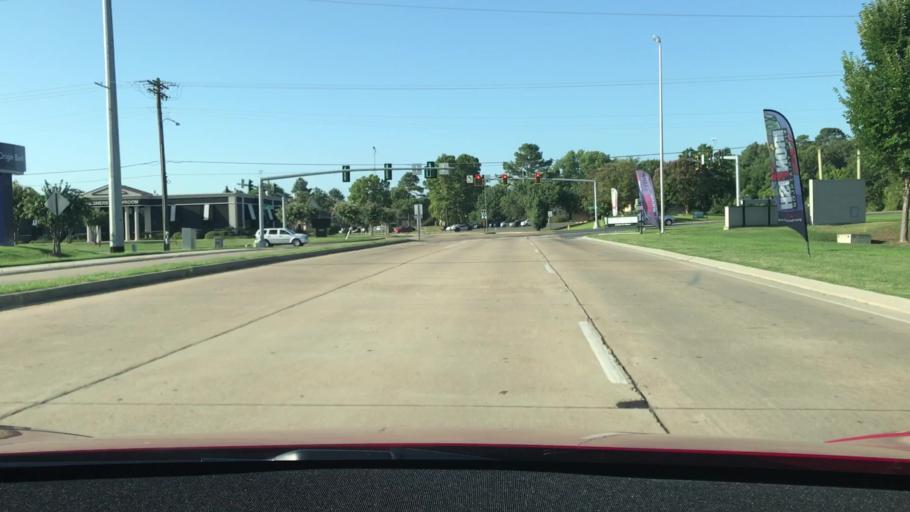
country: US
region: Louisiana
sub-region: Bossier Parish
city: Bossier City
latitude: 32.4442
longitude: -93.7298
